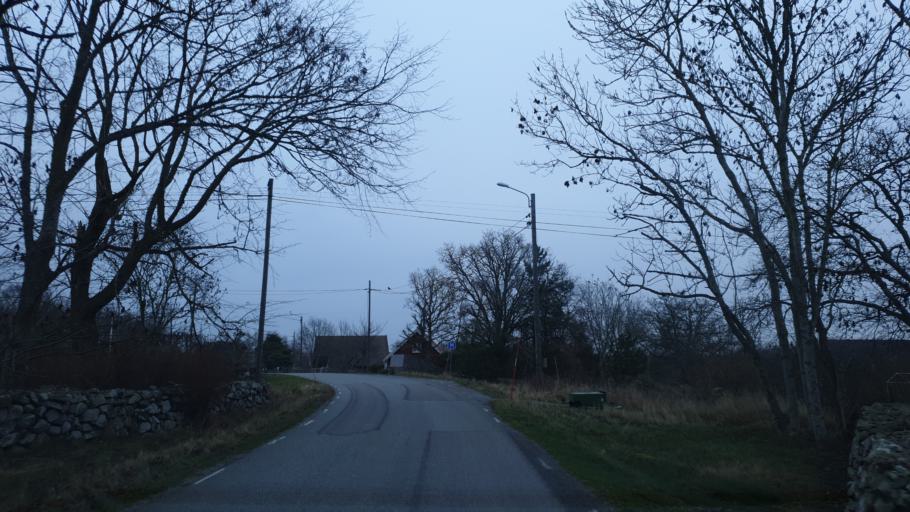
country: SE
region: Blekinge
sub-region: Karlskrona Kommun
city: Karlskrona
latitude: 56.1077
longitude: 15.6058
